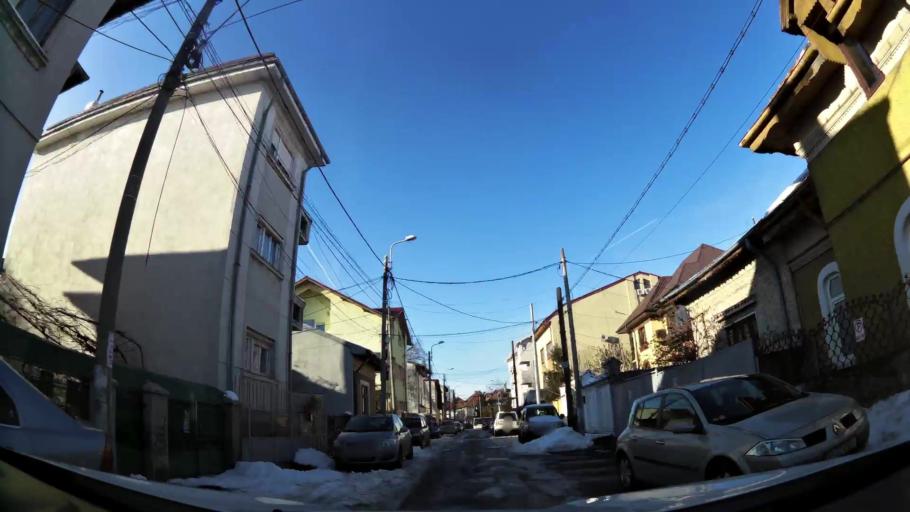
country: RO
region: Bucuresti
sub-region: Municipiul Bucuresti
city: Bucuresti
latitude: 44.4021
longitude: 26.0940
